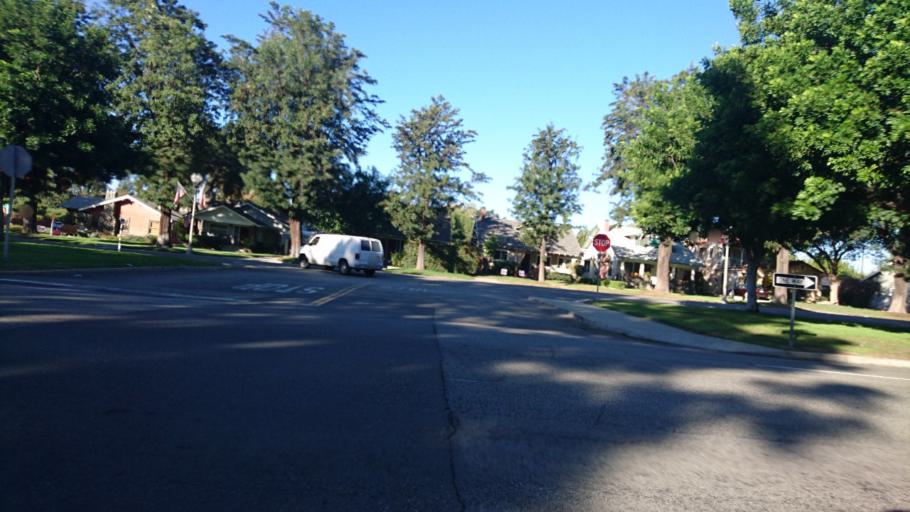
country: US
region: California
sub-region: San Bernardino County
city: Upland
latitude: 34.0985
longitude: -117.6509
